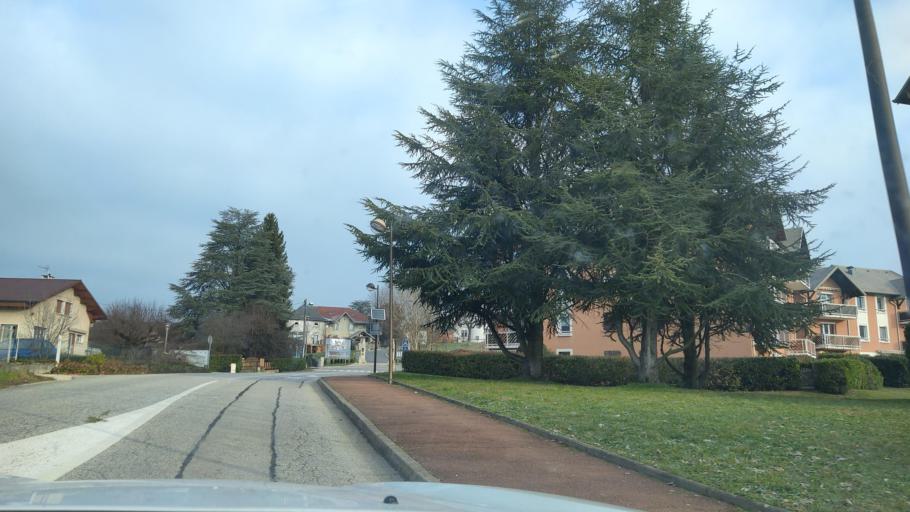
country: FR
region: Rhone-Alpes
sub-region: Departement de la Savoie
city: Gresy-sur-Aix
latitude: 45.7248
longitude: 5.9258
